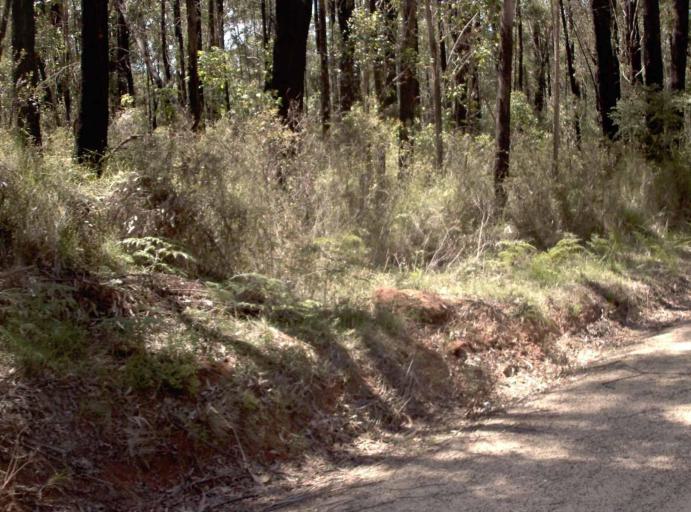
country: AU
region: New South Wales
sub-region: Bombala
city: Bombala
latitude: -37.5730
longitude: 149.0245
